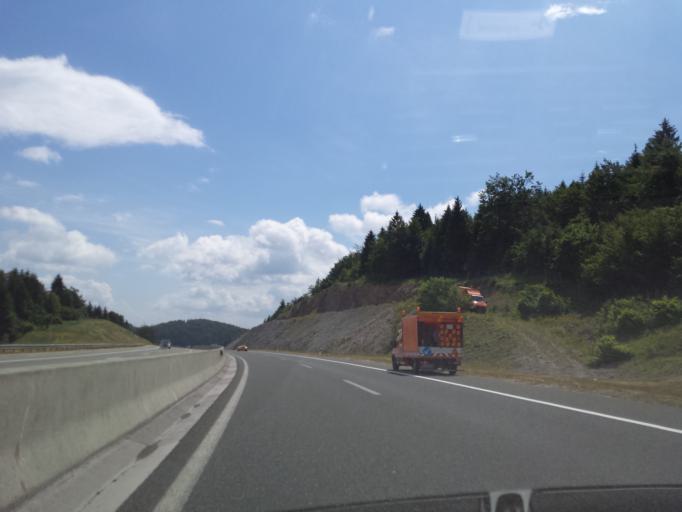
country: HR
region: Primorsko-Goranska
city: Vrbovsko
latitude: 45.3731
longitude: 14.9886
